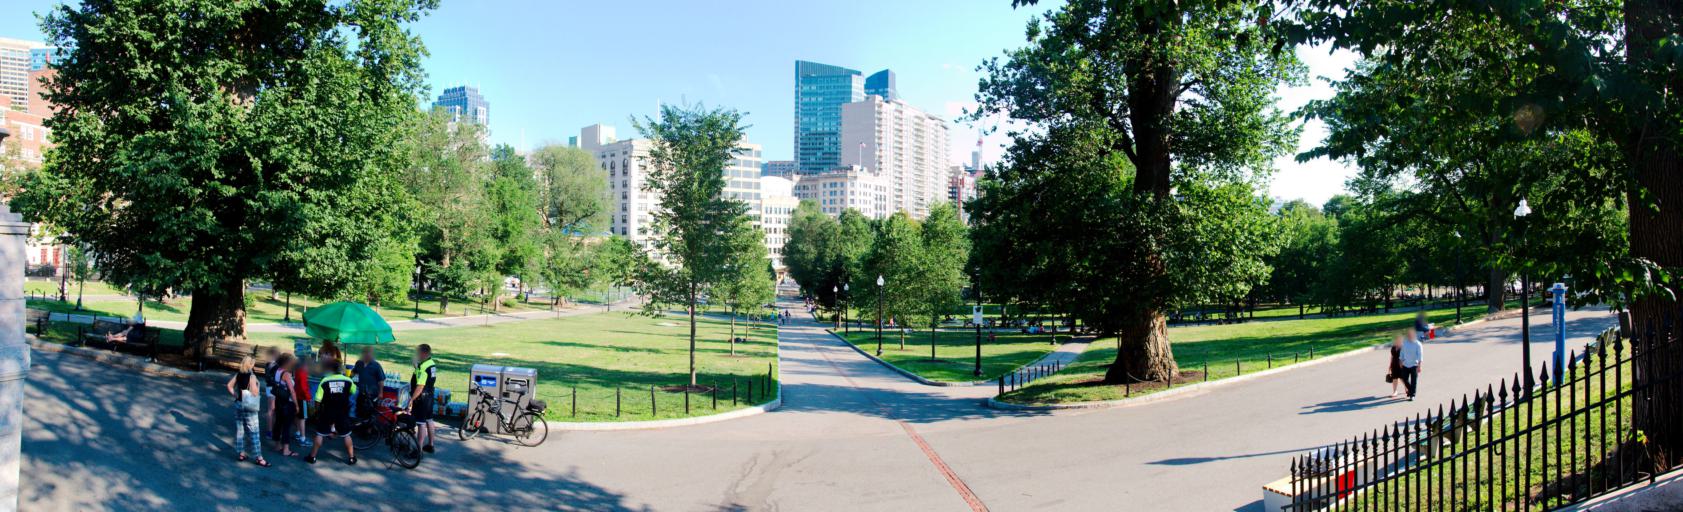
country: US
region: Massachusetts
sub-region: Suffolk County
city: Boston
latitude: 42.3574
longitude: -71.0637
